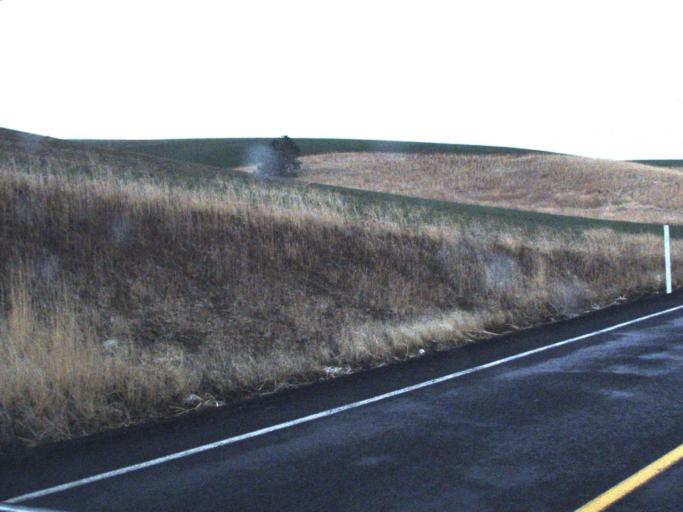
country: US
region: Washington
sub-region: Lincoln County
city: Davenport
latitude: 47.7279
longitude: -118.1588
